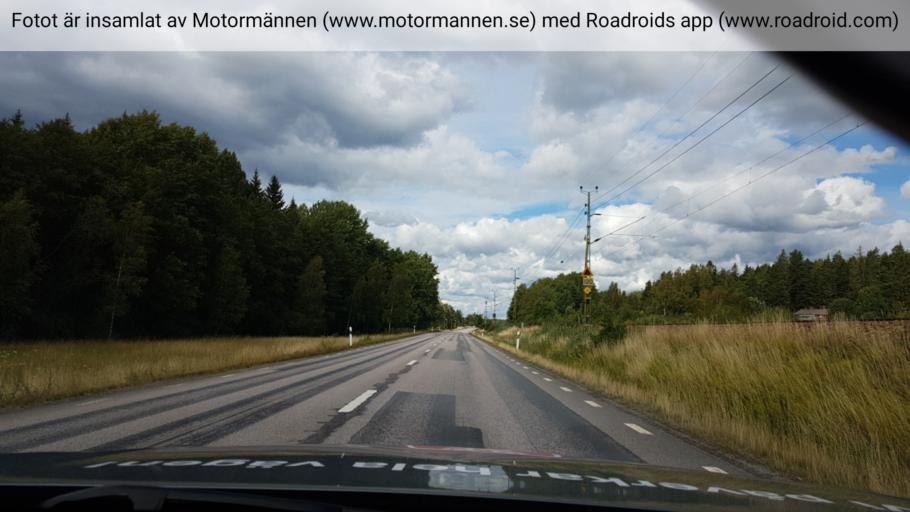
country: SE
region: Uppsala
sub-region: Heby Kommun
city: Morgongava
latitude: 59.9231
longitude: 16.9881
